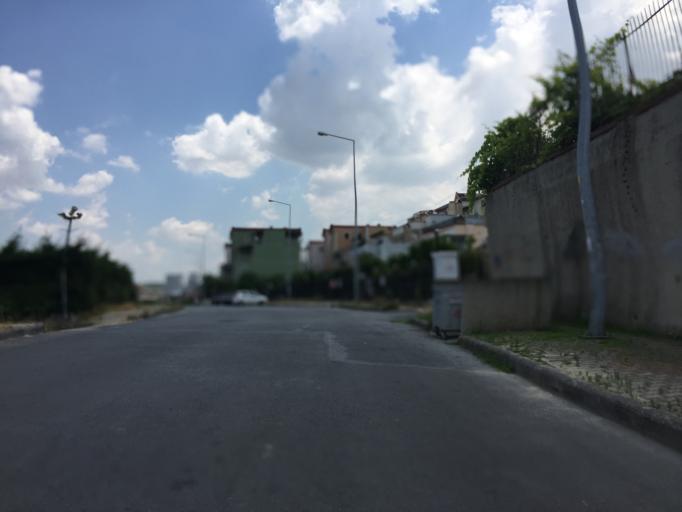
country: TR
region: Istanbul
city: Esenyurt
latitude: 41.0790
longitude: 28.6692
